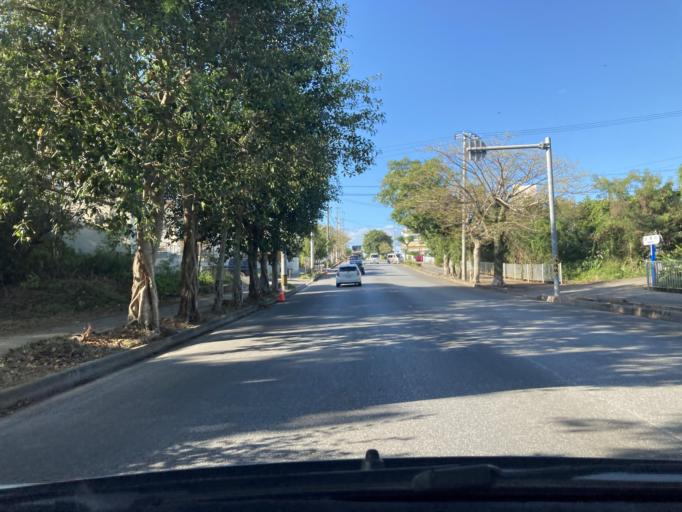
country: JP
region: Okinawa
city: Gushikawa
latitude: 26.3655
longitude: 127.8414
